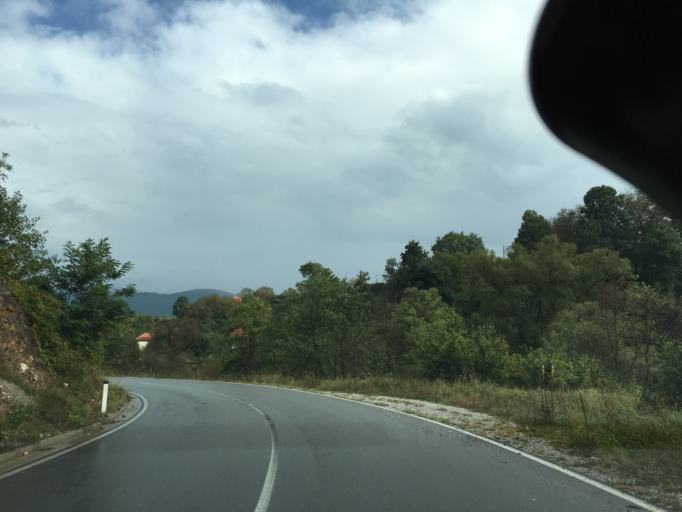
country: ME
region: Berane
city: Berane
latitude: 42.8277
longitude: 19.8383
